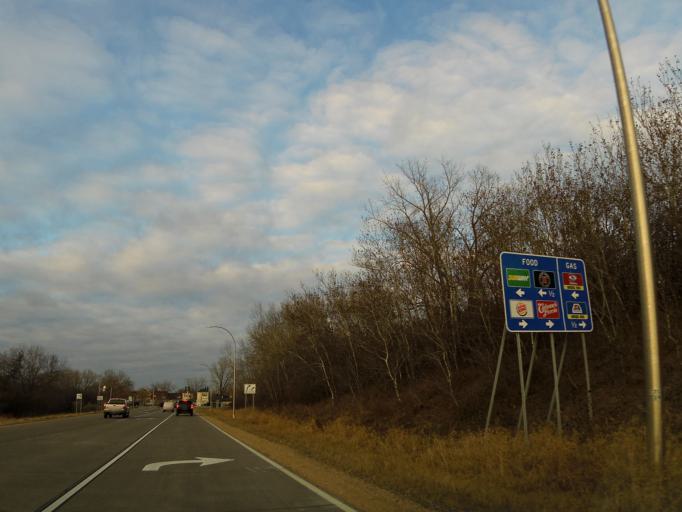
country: US
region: Minnesota
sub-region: Ramsey County
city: Vadnais Heights
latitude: 45.0776
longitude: -93.0522
